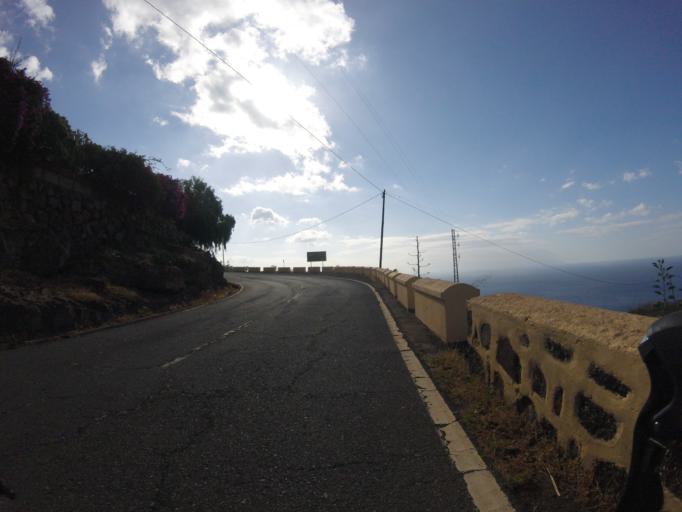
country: ES
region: Canary Islands
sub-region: Provincia de Santa Cruz de Tenerife
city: Candelaria
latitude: 28.3949
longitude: -16.3511
